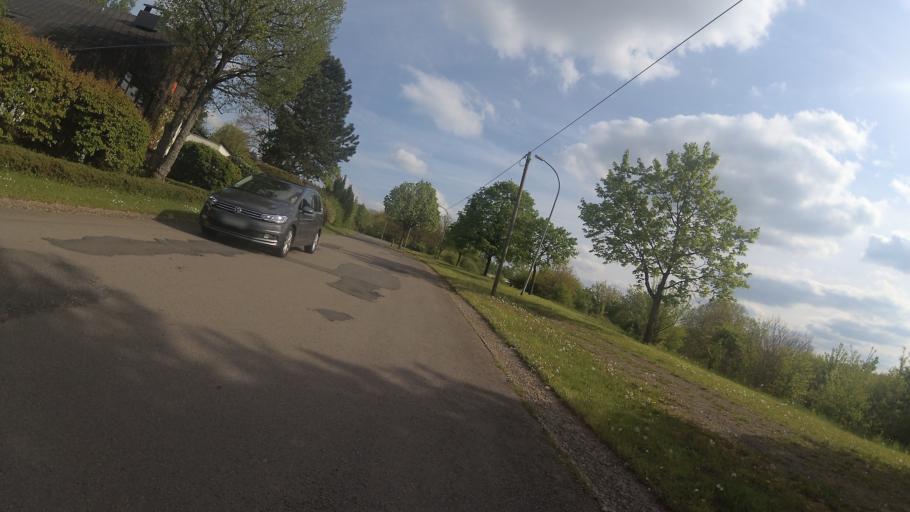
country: DE
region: Saarland
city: Sankt Wendel
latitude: 49.4605
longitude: 7.1820
